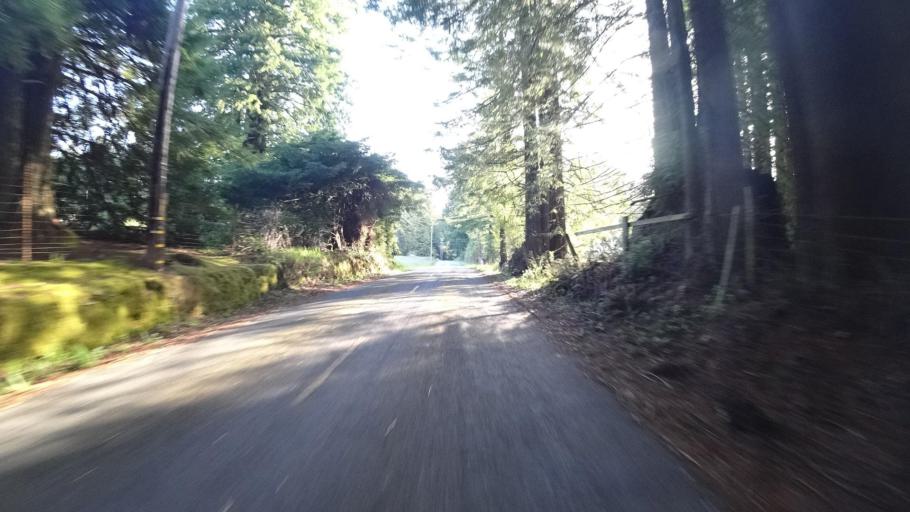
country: US
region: California
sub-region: Humboldt County
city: Myrtletown
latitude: 40.7708
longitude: -124.1183
